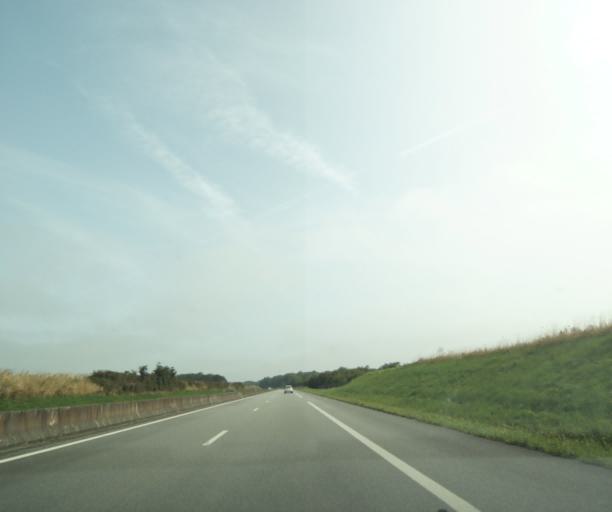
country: FR
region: Lower Normandy
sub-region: Departement de l'Orne
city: Sees
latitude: 48.5432
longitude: 0.1692
